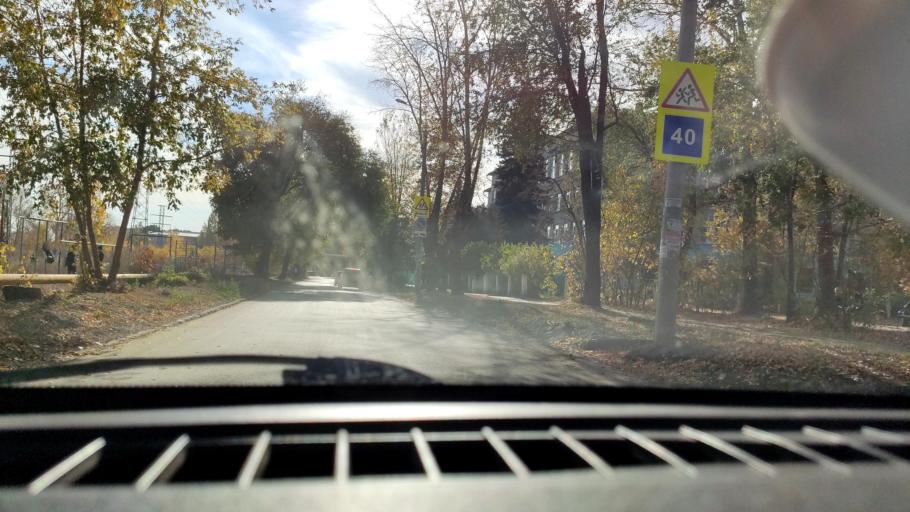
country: RU
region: Samara
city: Petra-Dubrava
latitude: 53.2976
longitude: 50.2905
